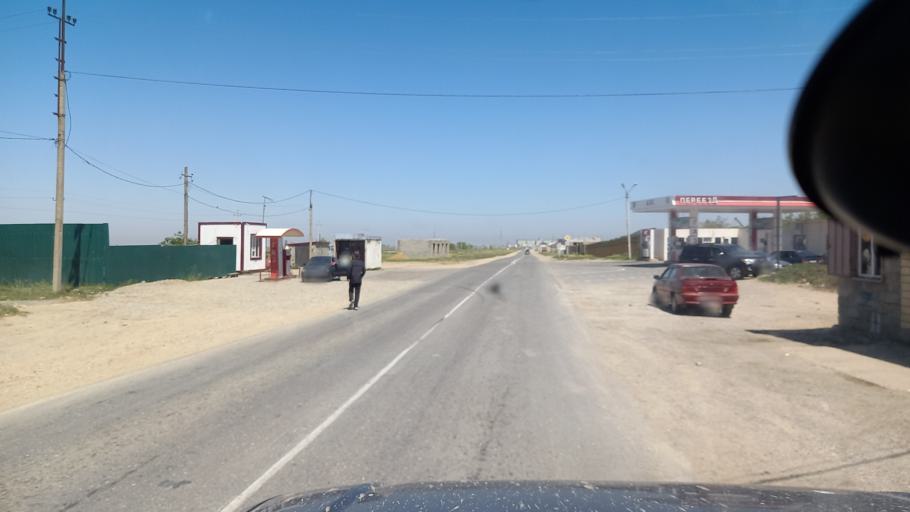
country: RU
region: Dagestan
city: Korkmaskala
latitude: 43.0291
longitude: 47.2669
